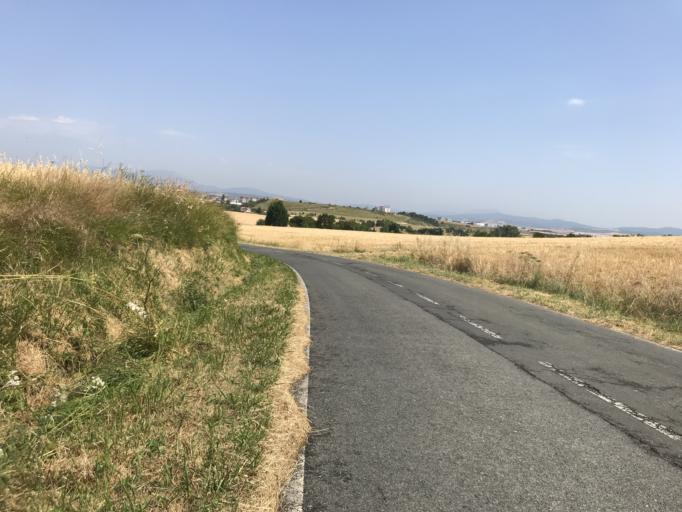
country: ES
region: Basque Country
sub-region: Provincia de Alava
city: Gasteiz / Vitoria
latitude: 42.8220
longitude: -2.6477
